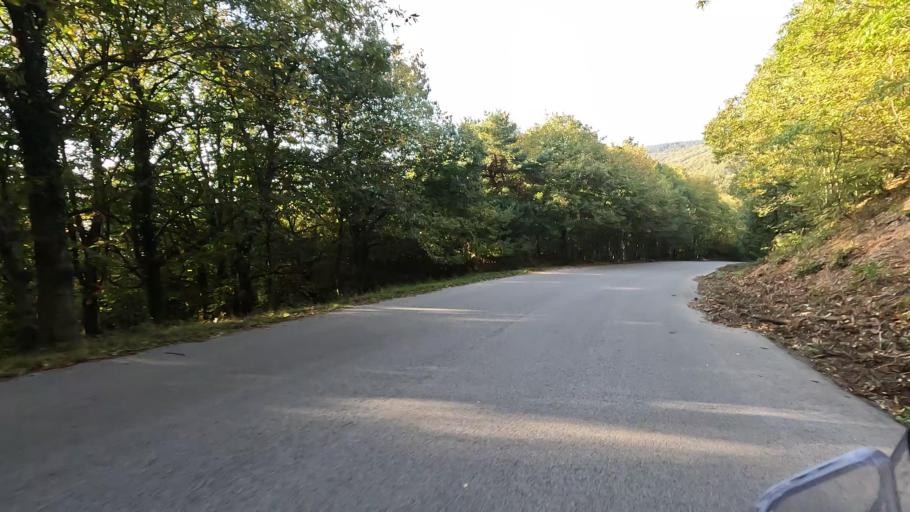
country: IT
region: Liguria
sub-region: Provincia di Savona
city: San Giovanni
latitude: 44.4120
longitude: 8.5272
